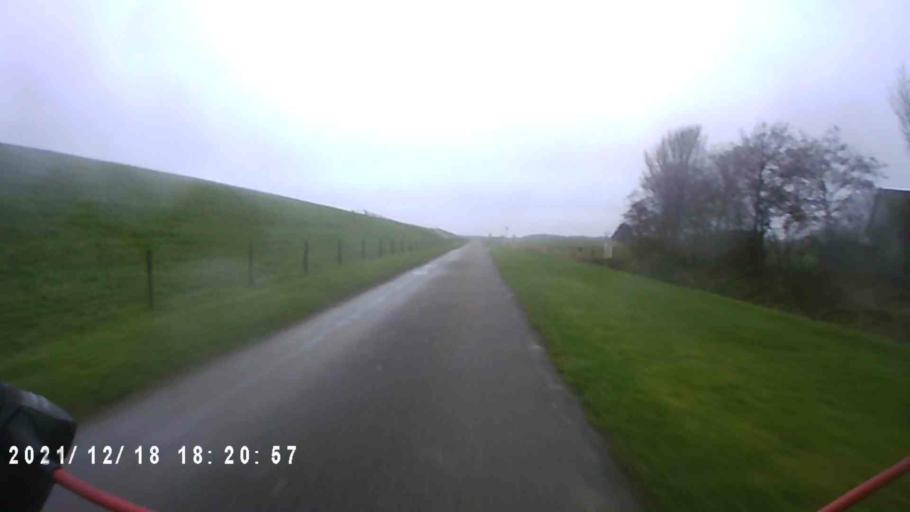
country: NL
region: Friesland
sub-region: Gemeente Dongeradeel
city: Ternaard
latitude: 53.3953
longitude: 5.9840
